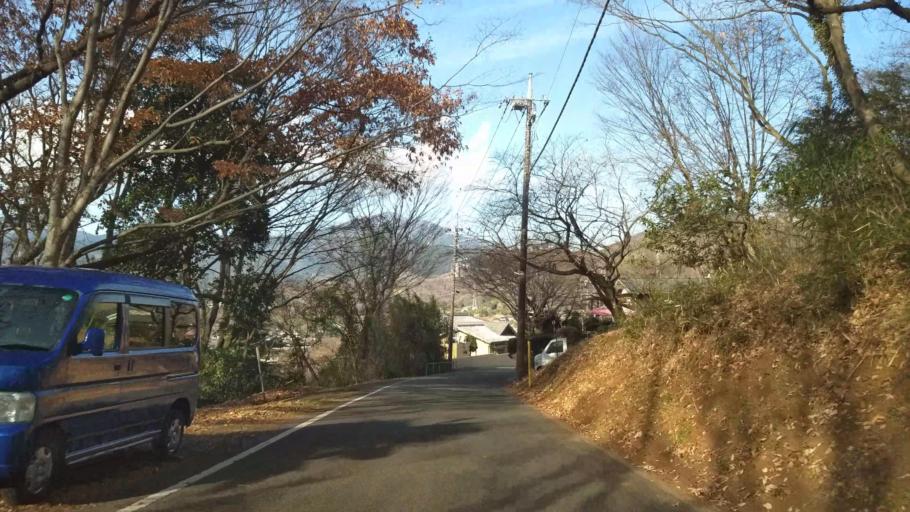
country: JP
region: Kanagawa
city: Hadano
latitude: 35.3766
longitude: 139.2448
